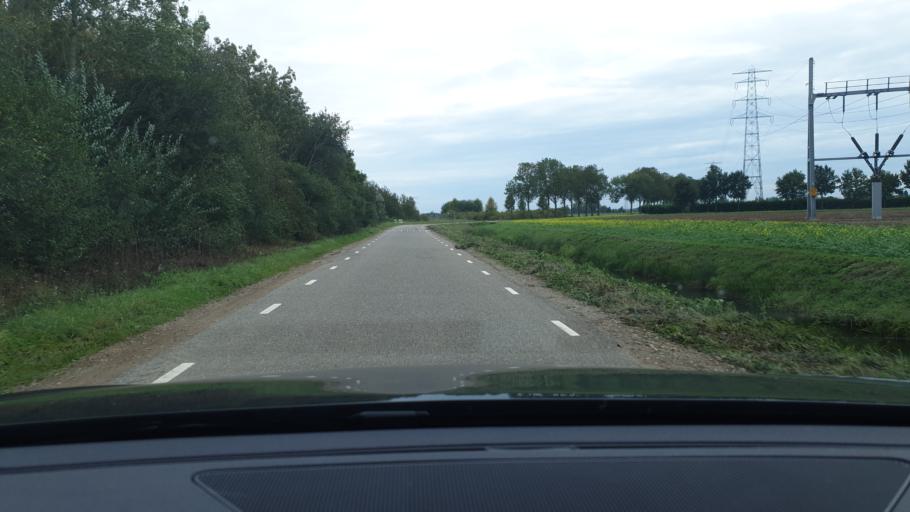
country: NL
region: Gelderland
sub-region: Gemeente Overbetuwe
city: Valburg
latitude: 51.8994
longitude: 5.7990
